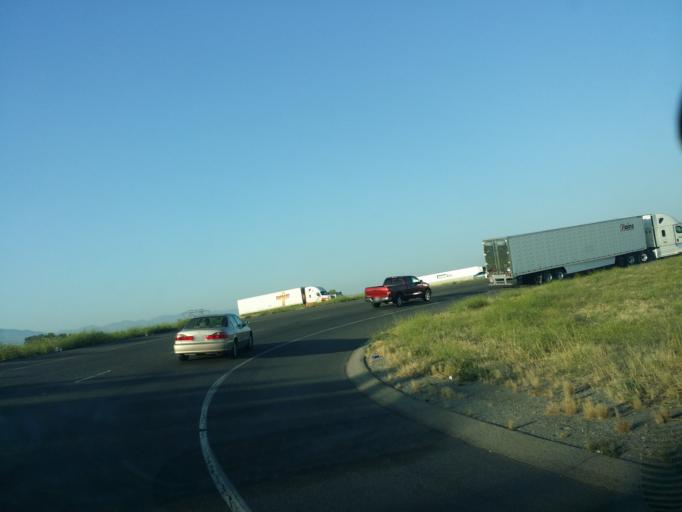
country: US
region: California
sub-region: San Bernardino County
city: Rancho Cucamonga
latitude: 34.0784
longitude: -117.5461
